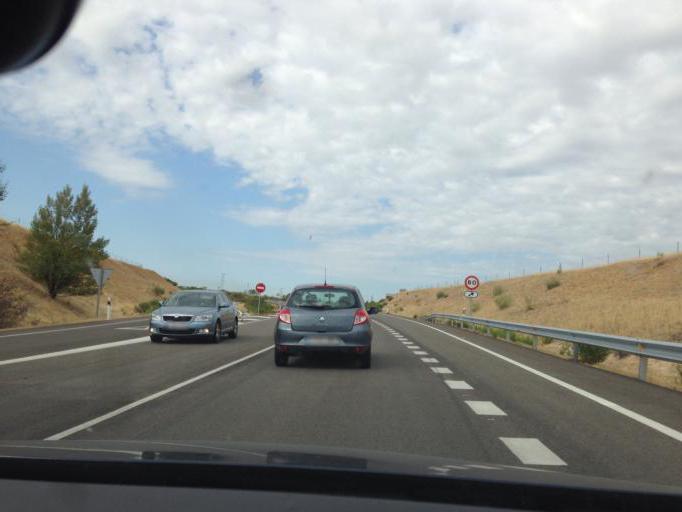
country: ES
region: Madrid
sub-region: Provincia de Madrid
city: Cobena
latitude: 40.5559
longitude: -3.4903
